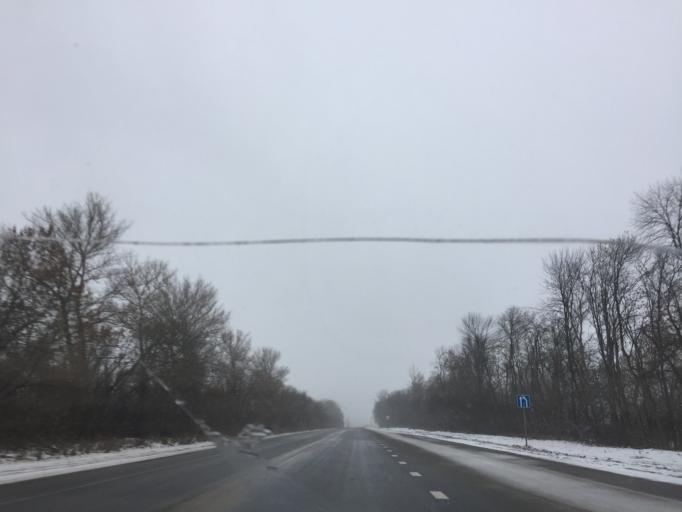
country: RU
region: Tula
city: Plavsk
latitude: 53.7318
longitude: 37.3082
